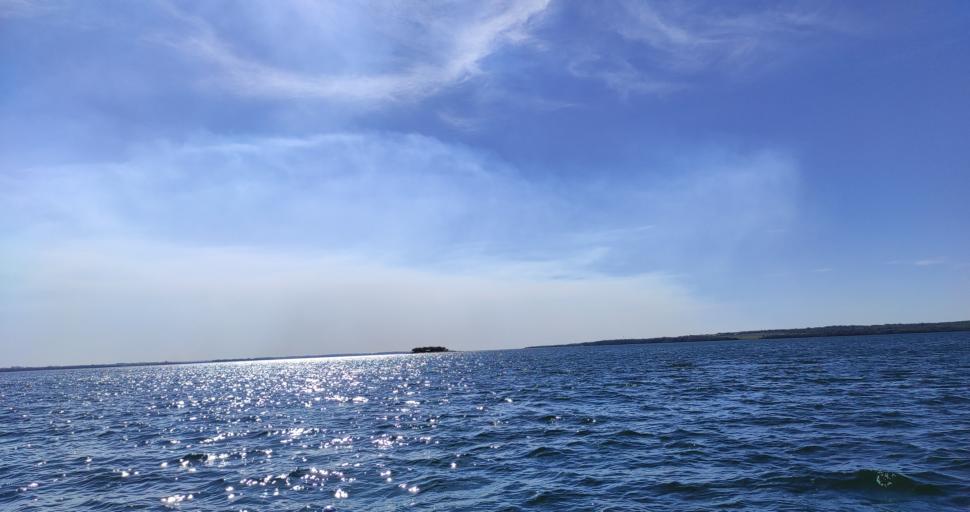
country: AR
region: Misiones
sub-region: Departamento de Capital
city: Posadas
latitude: -27.3433
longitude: -55.9347
